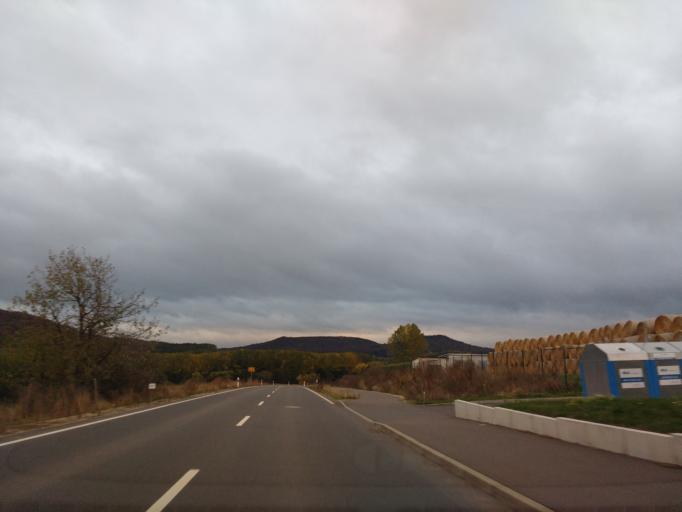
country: DE
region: Thuringia
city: Grossbodungen
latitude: 51.4662
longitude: 10.4641
